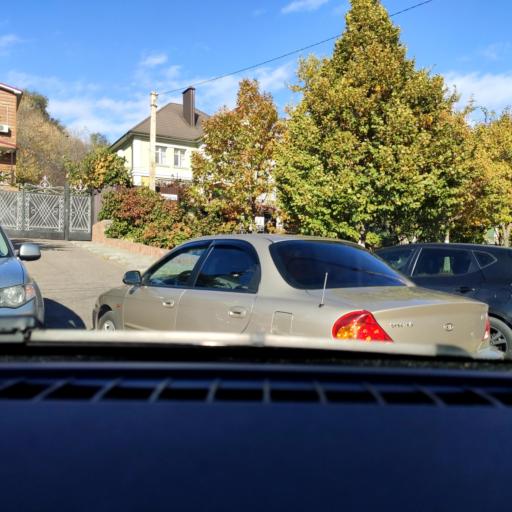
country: RU
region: Voronezj
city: Voronezh
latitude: 51.6533
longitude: 39.2096
